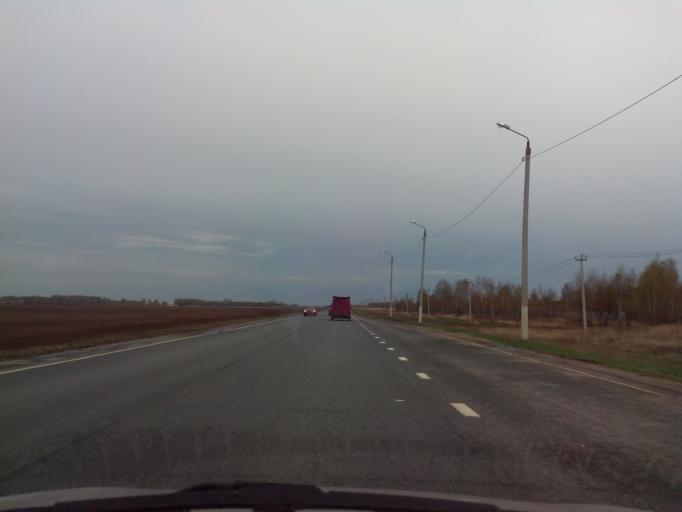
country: RU
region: Moskovskaya
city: Ozherel'ye
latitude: 54.6470
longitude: 38.3628
